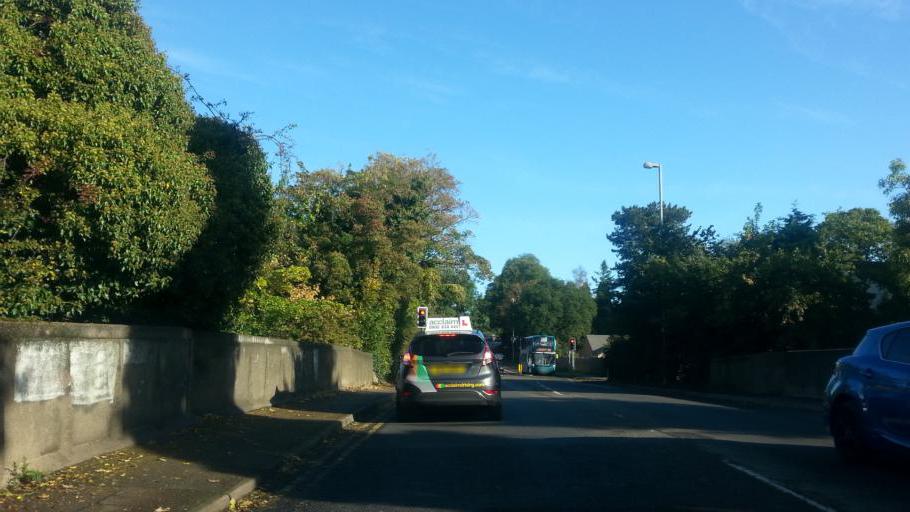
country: GB
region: England
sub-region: Leicestershire
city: Blaby
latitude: 52.5822
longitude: -1.1630
